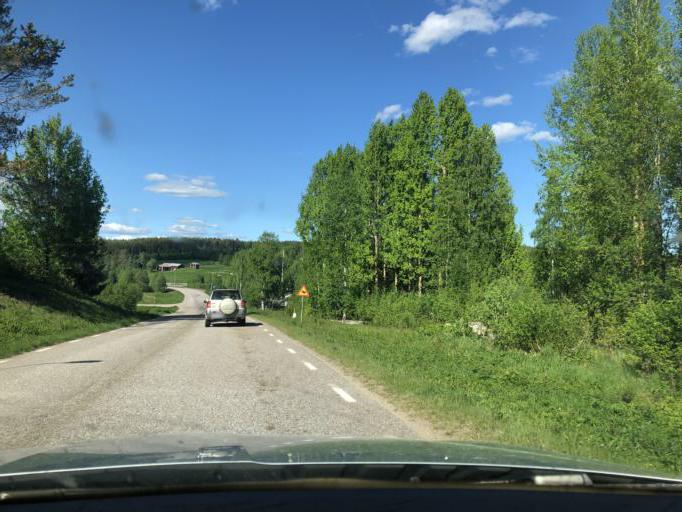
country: SE
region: Norrbotten
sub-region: Kalix Kommun
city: Kalix
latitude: 65.9897
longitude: 23.1485
